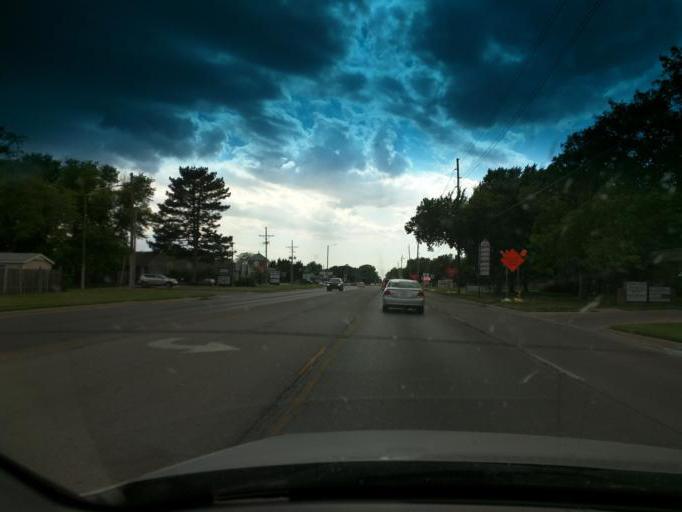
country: US
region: Kansas
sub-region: Reno County
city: Hutchinson
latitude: 38.0866
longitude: -97.9269
